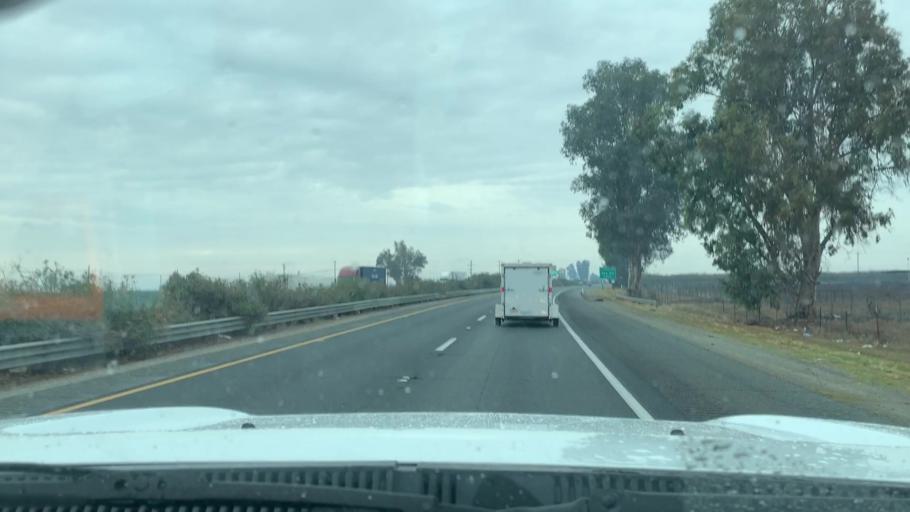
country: US
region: California
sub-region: Kern County
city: Delano
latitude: 35.8164
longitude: -119.2583
